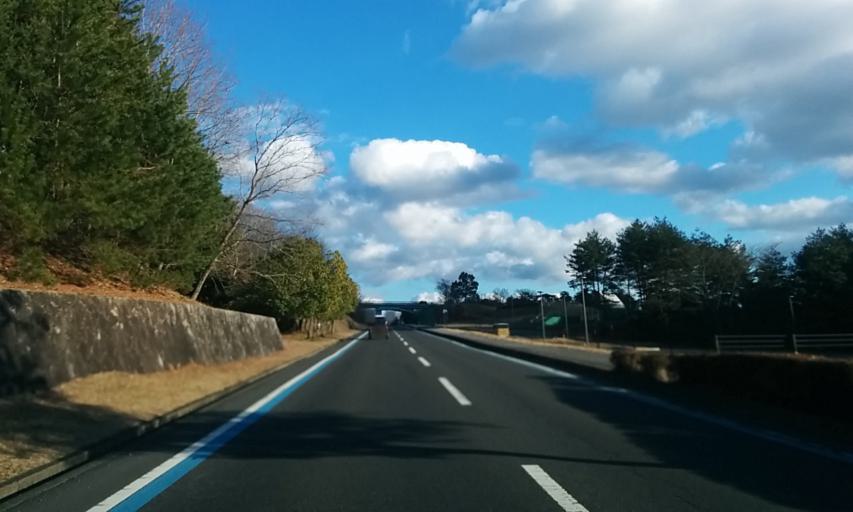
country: JP
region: Kyoto
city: Fukuchiyama
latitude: 35.3162
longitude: 135.1321
